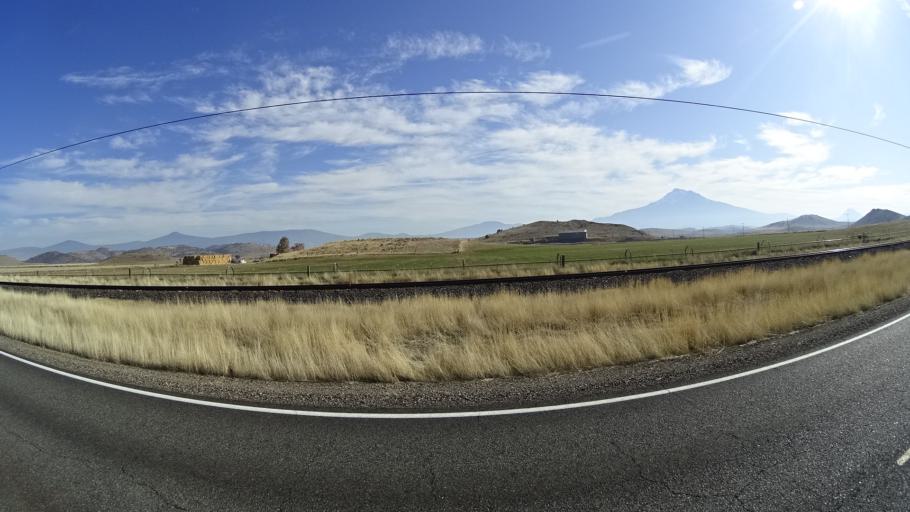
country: US
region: California
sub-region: Siskiyou County
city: Montague
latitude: 41.5634
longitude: -122.5258
